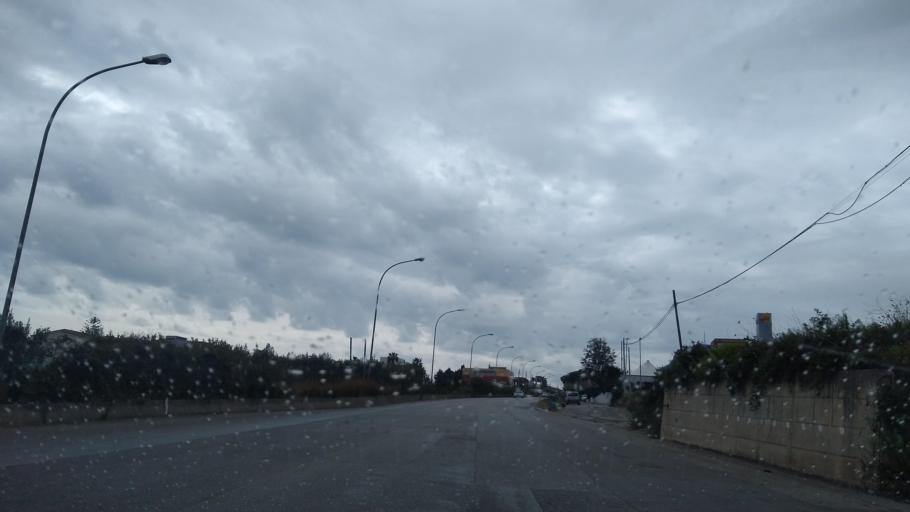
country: IT
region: Sicily
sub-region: Trapani
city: Alcamo
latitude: 37.9990
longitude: 12.9574
